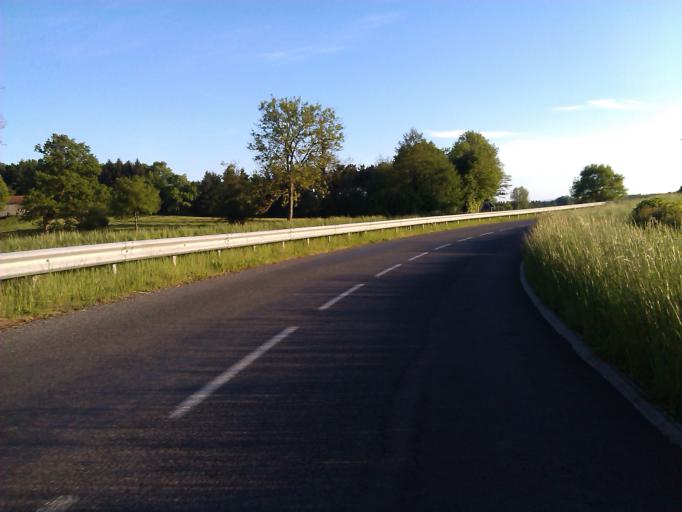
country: FR
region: Bourgogne
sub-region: Departement de Saone-et-Loire
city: Palinges
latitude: 46.5435
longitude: 4.2102
